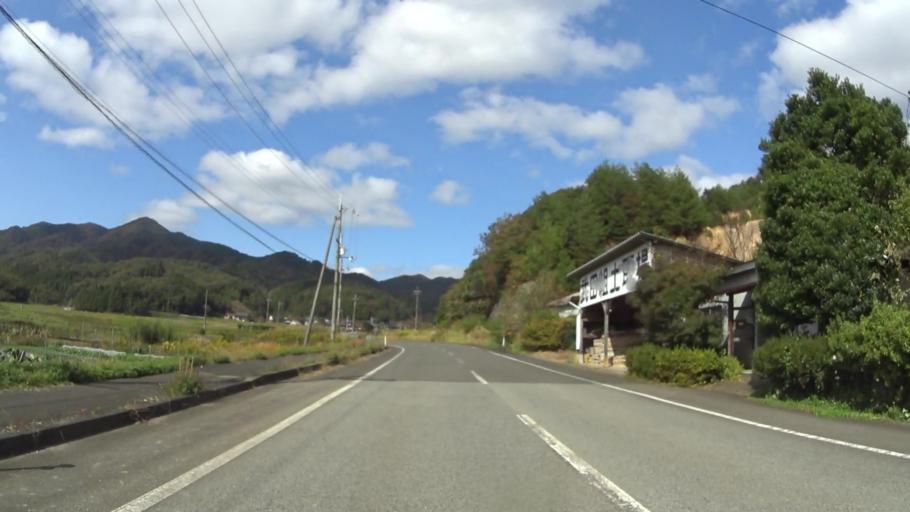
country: JP
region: Hyogo
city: Toyooka
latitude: 35.5031
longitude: 134.9926
